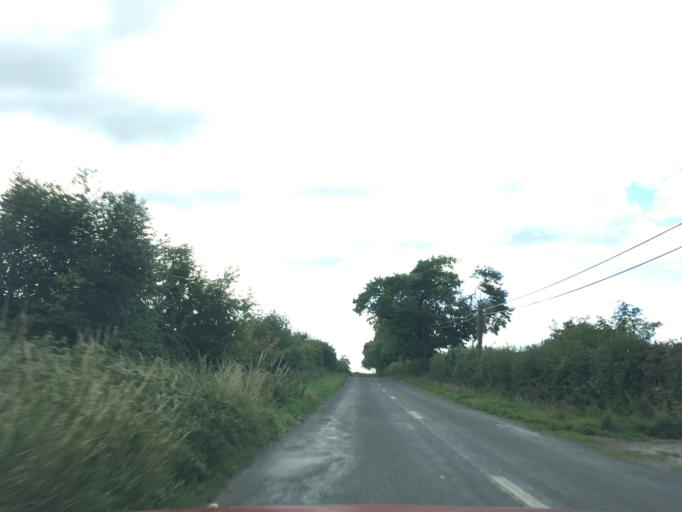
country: IE
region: Munster
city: Cashel
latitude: 52.4483
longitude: -7.9037
